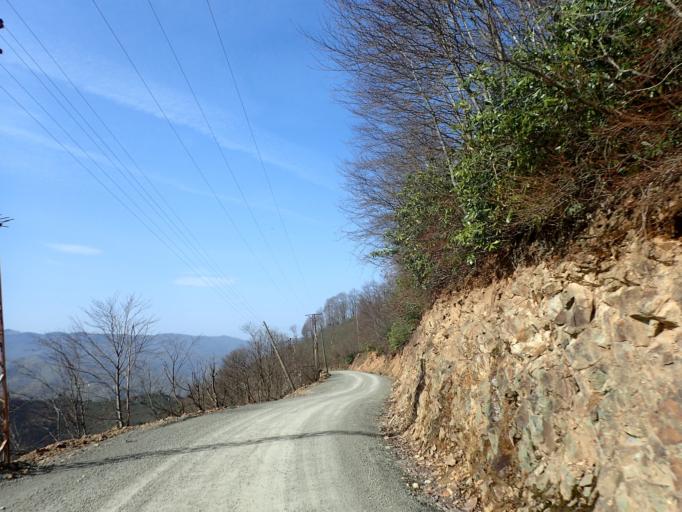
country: TR
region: Ordu
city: Kabaduz
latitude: 40.8174
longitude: 37.8948
